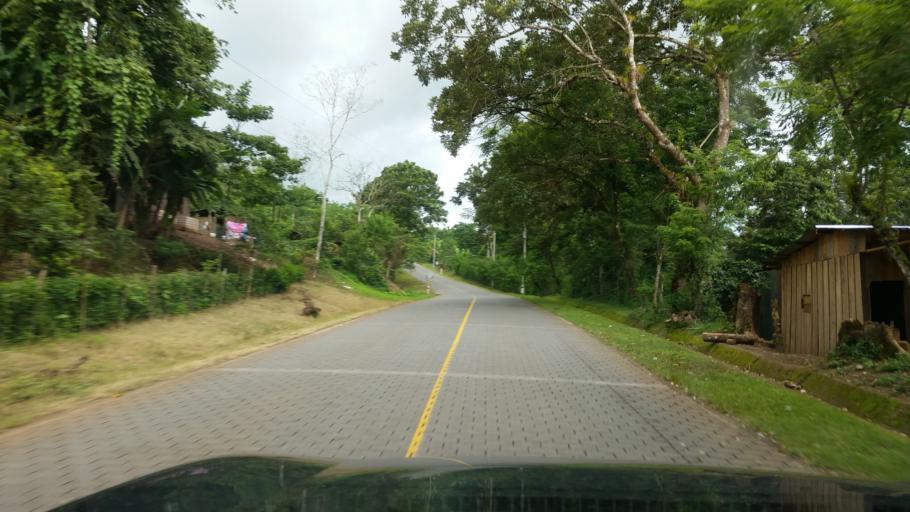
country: NI
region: Jinotega
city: Jinotega
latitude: 13.2063
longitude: -85.7230
